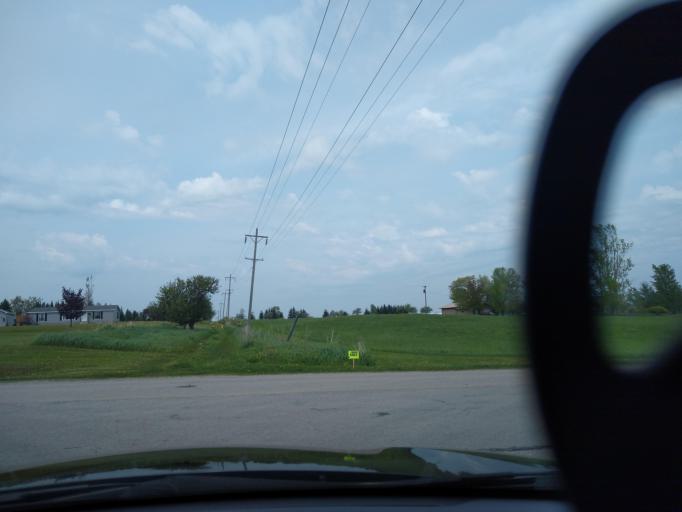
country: US
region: Michigan
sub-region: Delta County
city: Escanaba
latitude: 45.8260
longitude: -87.1415
